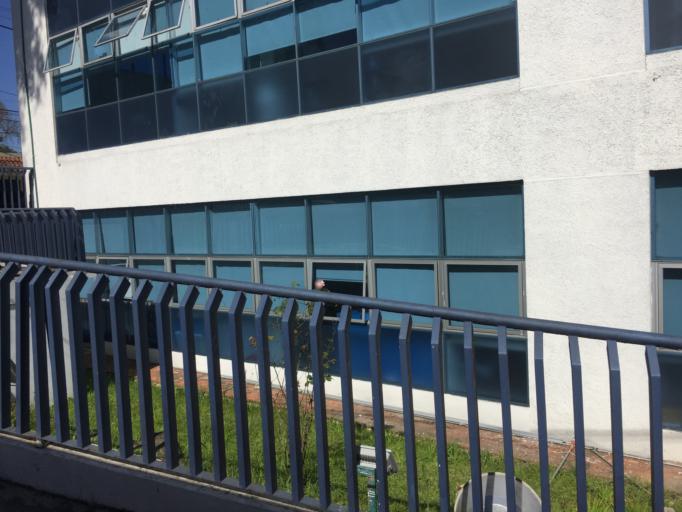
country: MX
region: Veracruz
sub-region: Xalapa
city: Xalapa de Enriquez
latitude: 19.5405
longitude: -96.9209
